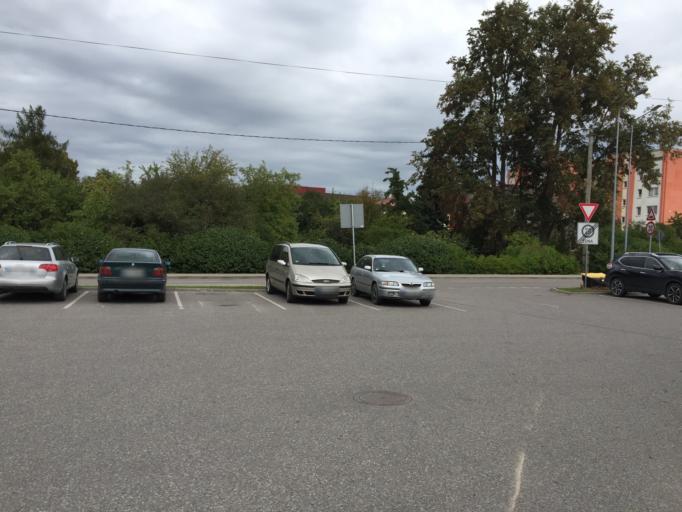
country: LV
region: Limbazu Rajons
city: Limbazi
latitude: 57.5085
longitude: 24.7143
